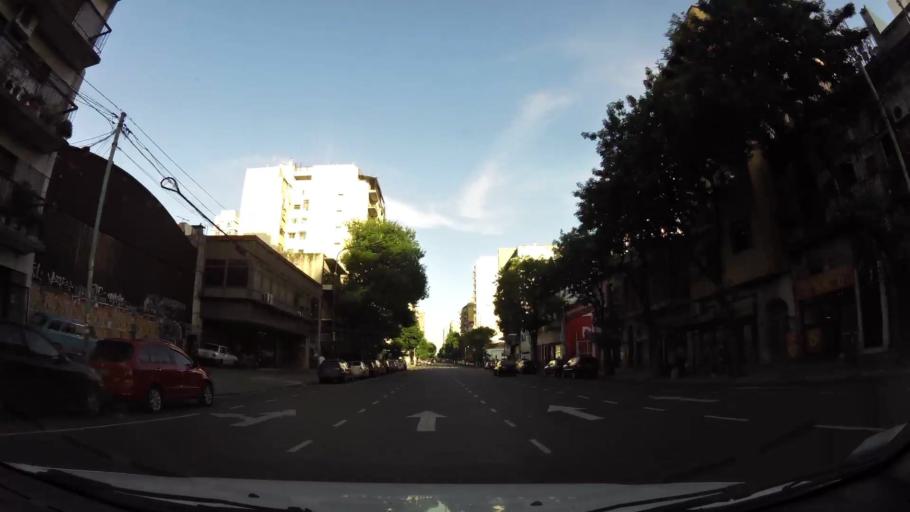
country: AR
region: Buenos Aires F.D.
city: Colegiales
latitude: -34.6087
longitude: -58.4302
